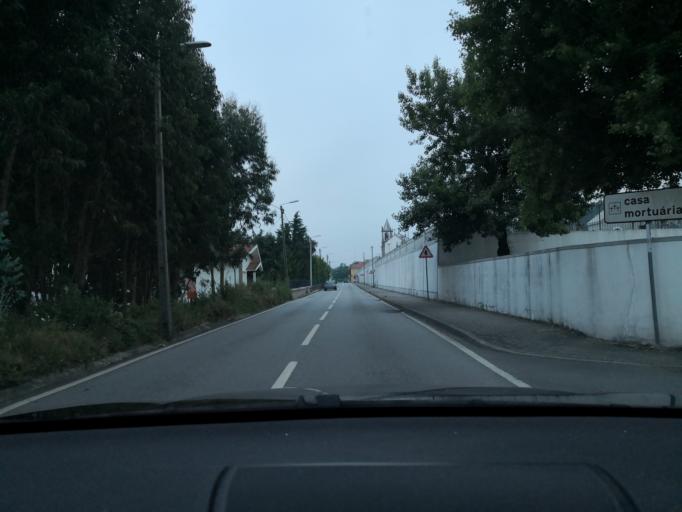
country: PT
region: Aveiro
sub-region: Santa Maria da Feira
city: Lamas
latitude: 41.0029
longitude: -8.5641
